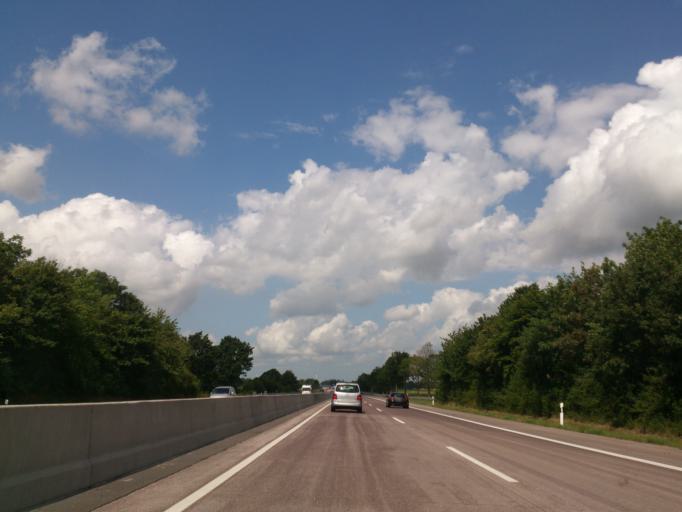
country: DE
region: Schleswig-Holstein
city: Horst
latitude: 53.8294
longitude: 9.6316
